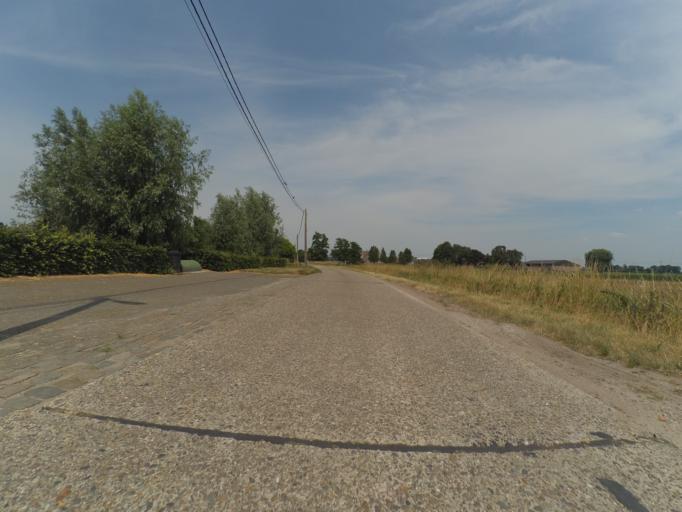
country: BE
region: Flanders
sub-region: Provincie Antwerpen
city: Brecht
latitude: 51.3863
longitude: 4.6331
